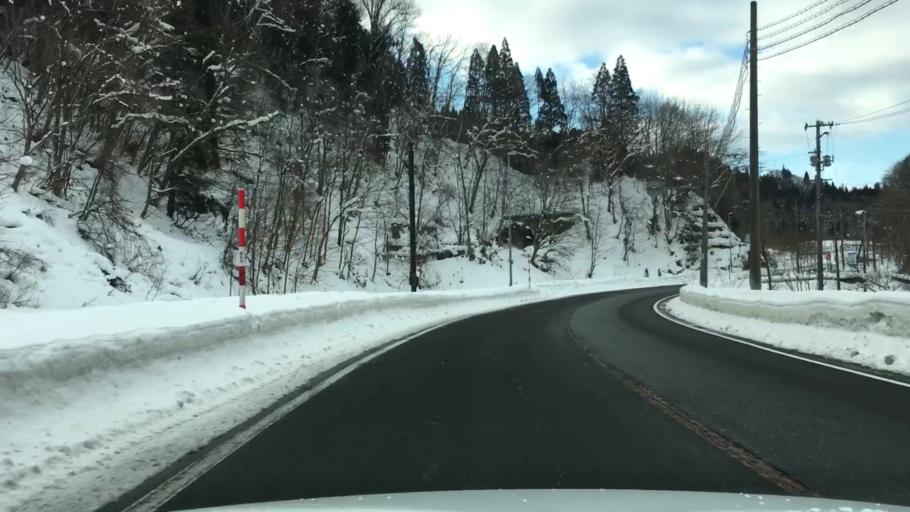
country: JP
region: Akita
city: Odate
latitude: 40.4271
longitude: 140.6364
